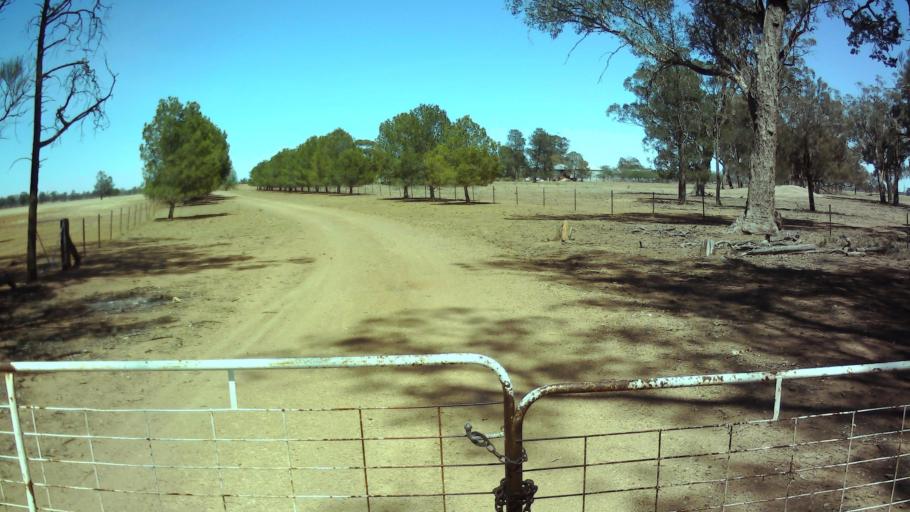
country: AU
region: New South Wales
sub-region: Weddin
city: Grenfell
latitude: -34.0919
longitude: 147.8845
